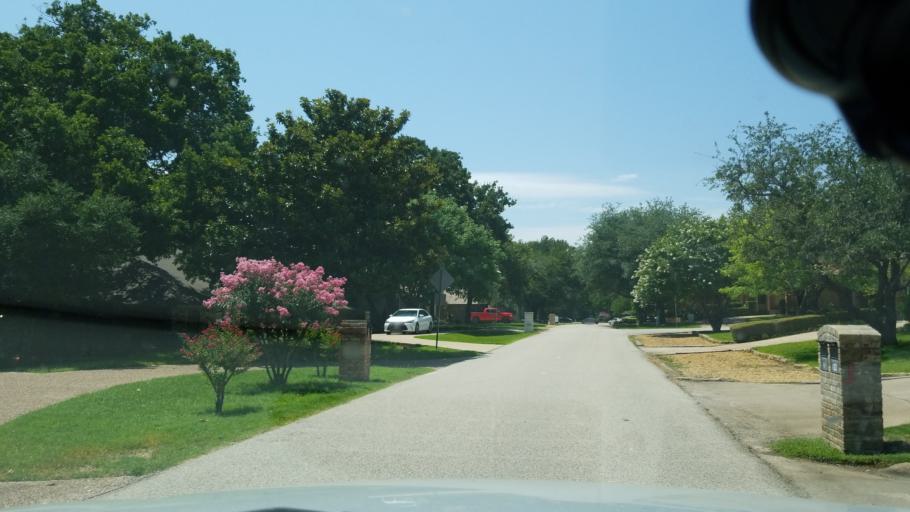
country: US
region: Texas
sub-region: Dallas County
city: Coppell
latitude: 32.9556
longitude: -96.9918
